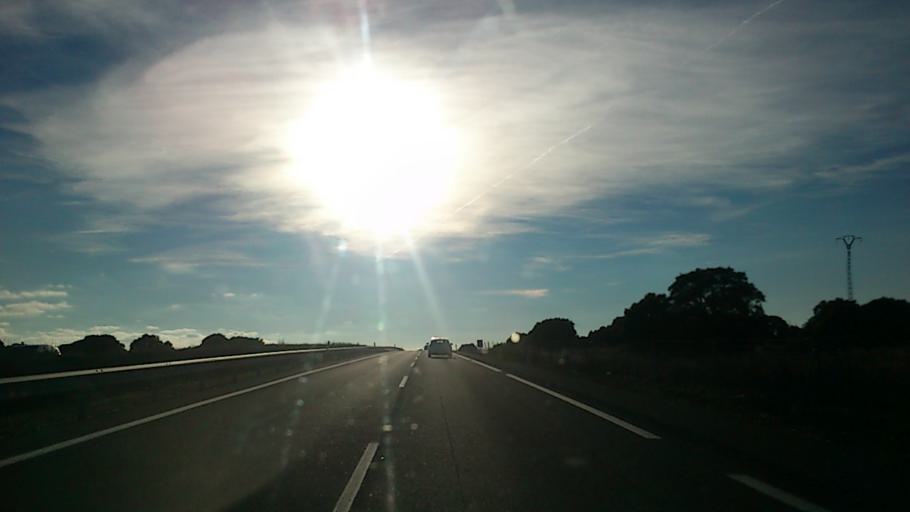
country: ES
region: Castille-La Mancha
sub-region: Provincia de Guadalajara
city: Mirabueno
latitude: 40.9423
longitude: -2.6975
